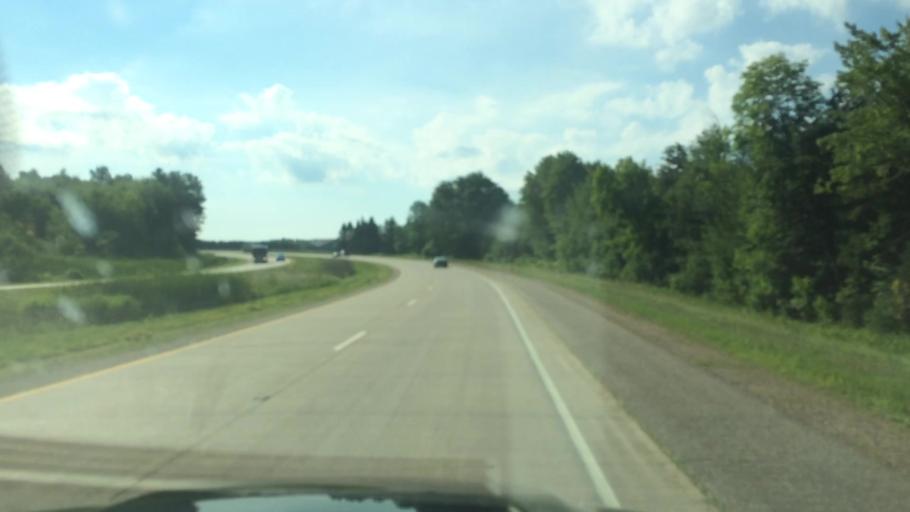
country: US
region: Wisconsin
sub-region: Shawano County
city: Wittenberg
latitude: 44.8057
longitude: -89.0347
